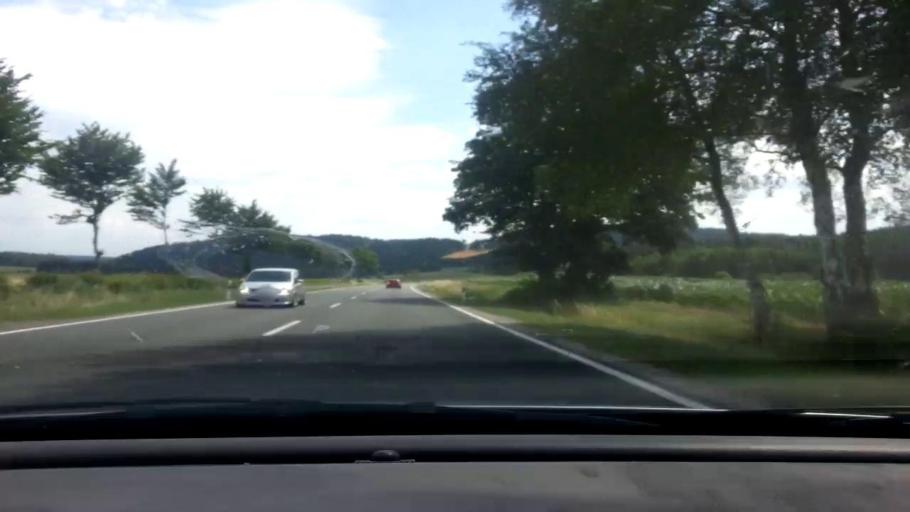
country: DE
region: Bavaria
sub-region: Upper Palatinate
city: Erbendorf
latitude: 49.8508
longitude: 11.9881
